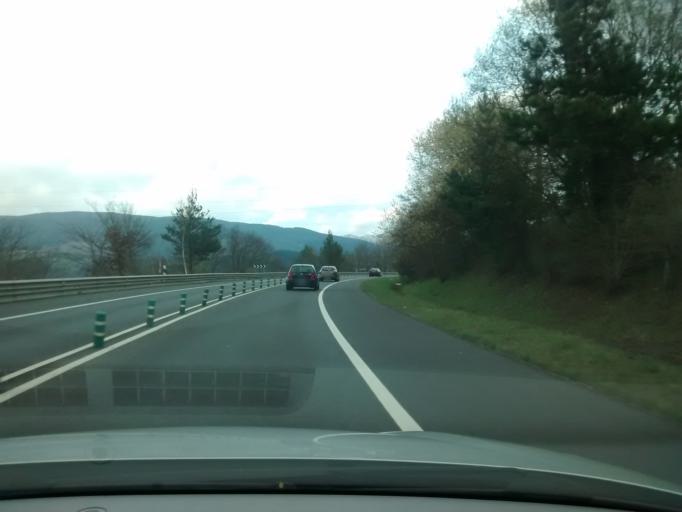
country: ES
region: Basque Country
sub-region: Bizkaia
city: El Corrillo
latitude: 43.2041
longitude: -3.1402
